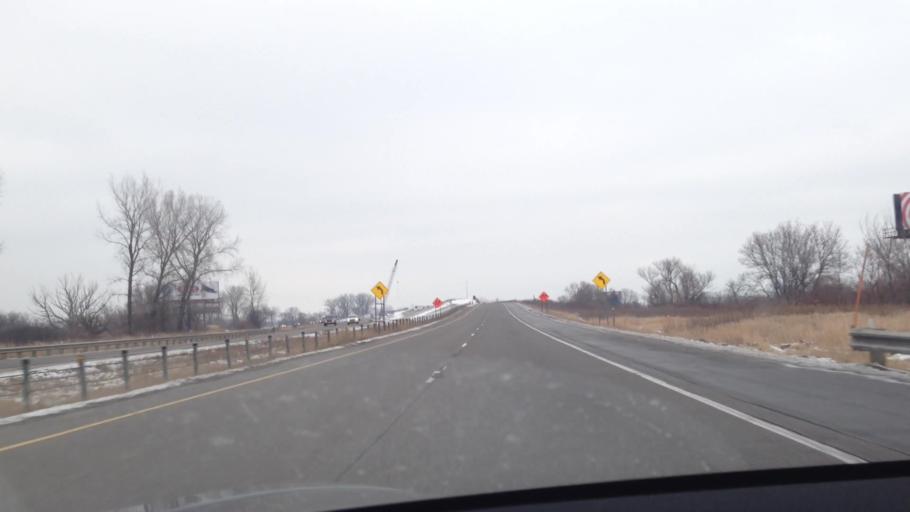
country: US
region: Minnesota
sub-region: Anoka County
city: Columbus
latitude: 45.2152
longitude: -93.0335
